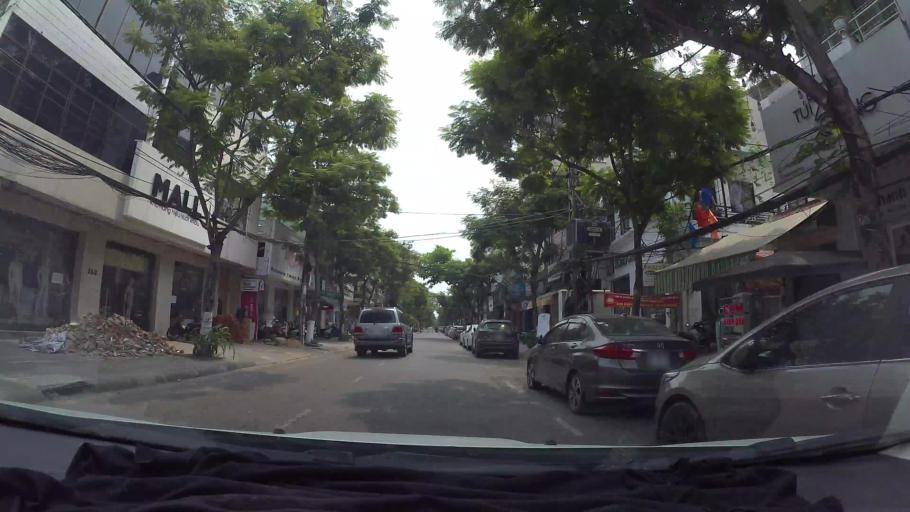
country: VN
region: Da Nang
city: Da Nang
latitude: 16.0601
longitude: 108.2194
